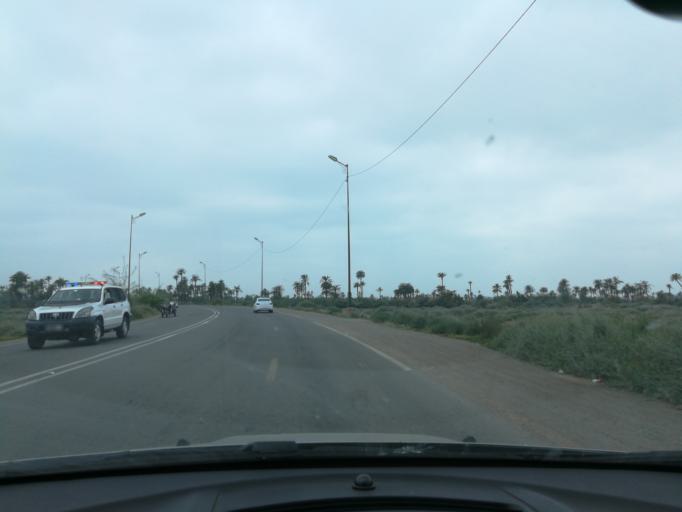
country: MA
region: Marrakech-Tensift-Al Haouz
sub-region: Marrakech
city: Marrakesh
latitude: 31.6908
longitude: -8.0146
